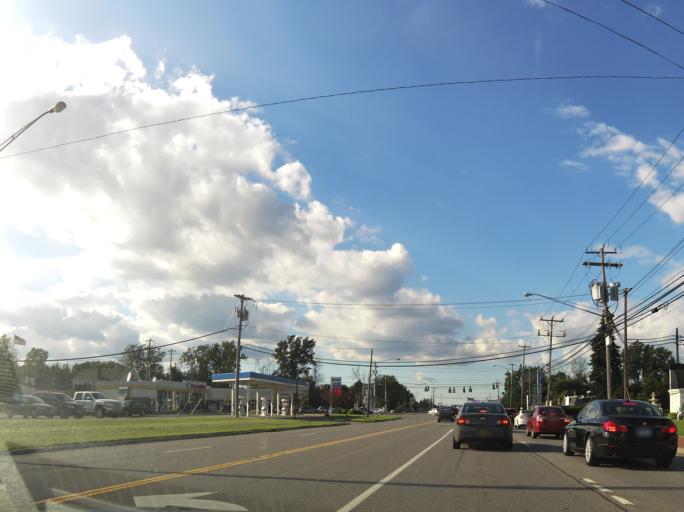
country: US
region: New York
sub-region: Erie County
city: Depew
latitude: 42.9368
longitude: -78.6969
